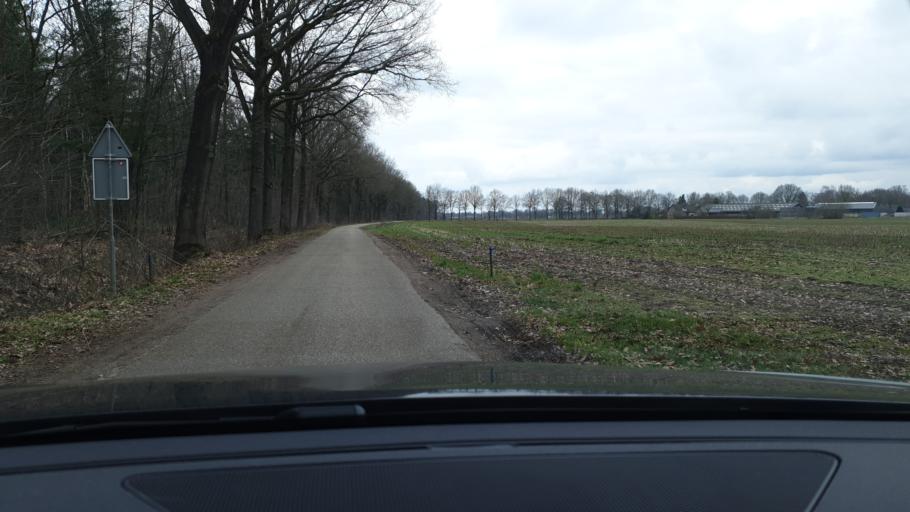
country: NL
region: North Brabant
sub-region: Gemeente Veldhoven
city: Oerle
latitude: 51.4256
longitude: 5.3379
